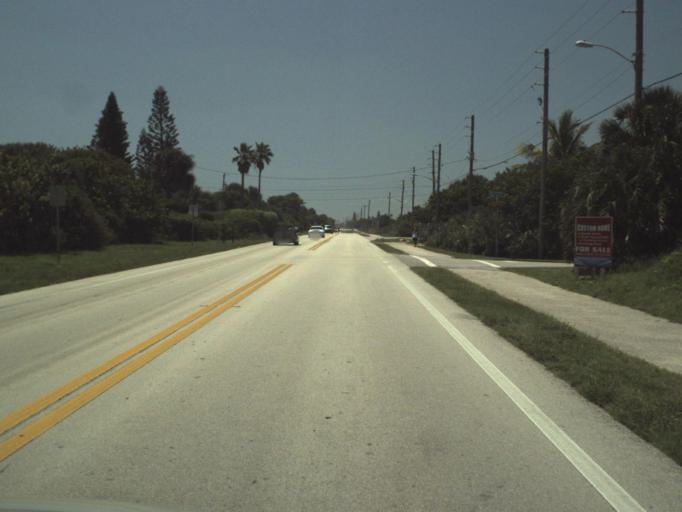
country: US
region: Florida
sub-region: Brevard County
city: Malabar
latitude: 28.0262
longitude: -80.5380
